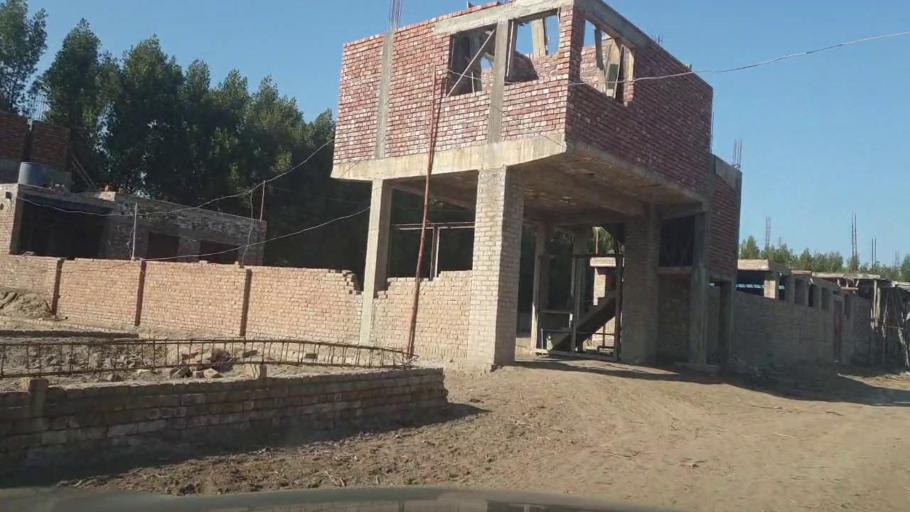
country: PK
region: Sindh
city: Mirpur Mathelo
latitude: 28.1396
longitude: 69.5965
